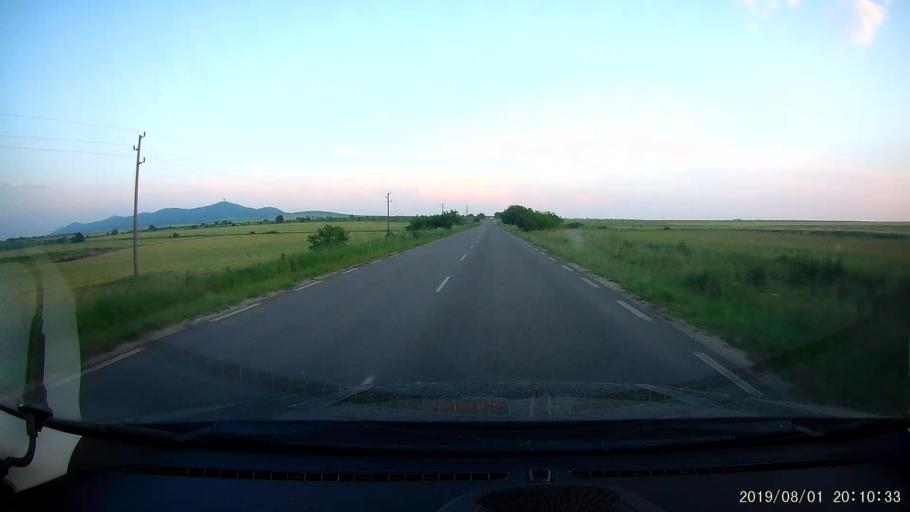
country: BG
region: Yambol
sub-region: Obshtina Yambol
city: Yambol
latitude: 42.4793
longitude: 26.6003
